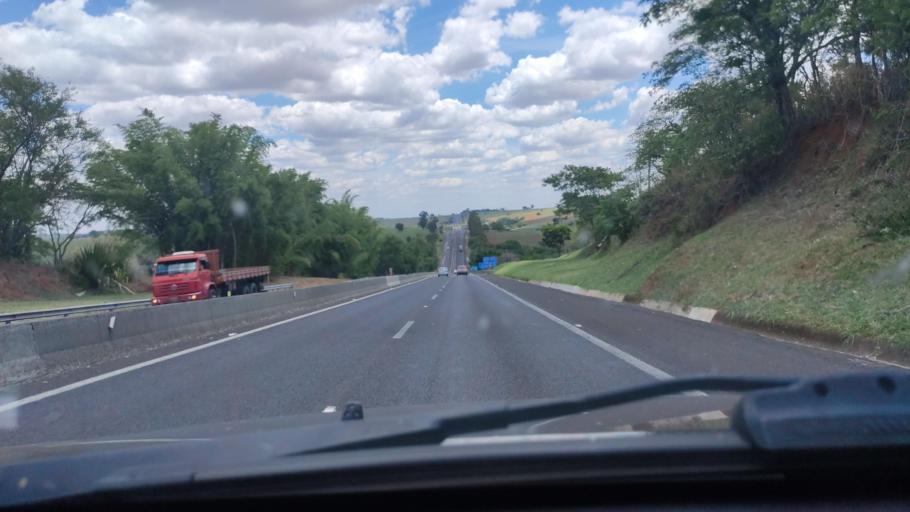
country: BR
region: Sao Paulo
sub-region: Santa Cruz Do Rio Pardo
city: Santa Cruz do Rio Pardo
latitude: -22.7416
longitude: -49.4713
